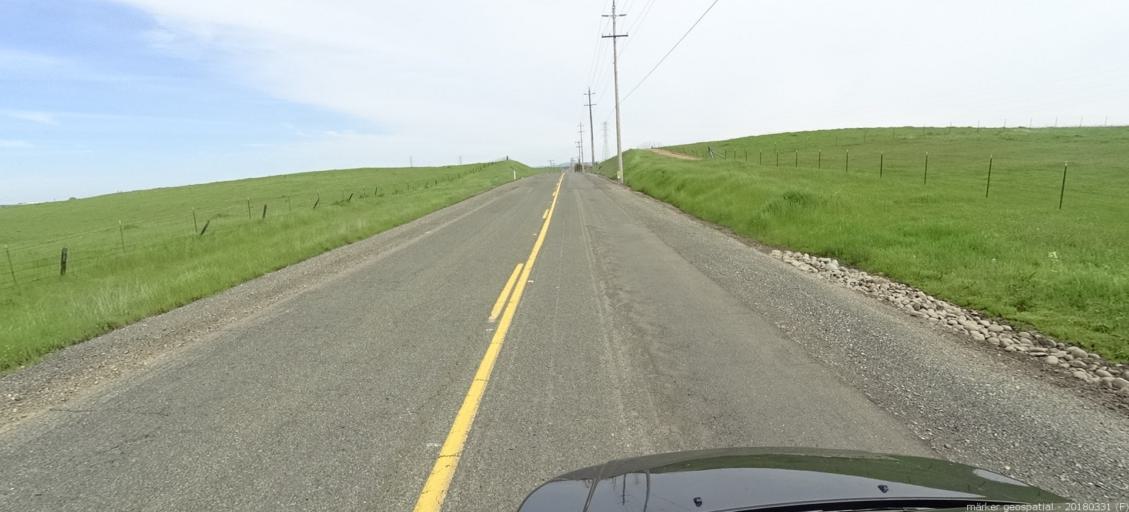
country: US
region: California
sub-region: Sacramento County
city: Rancho Murieta
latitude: 38.4998
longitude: -121.1440
